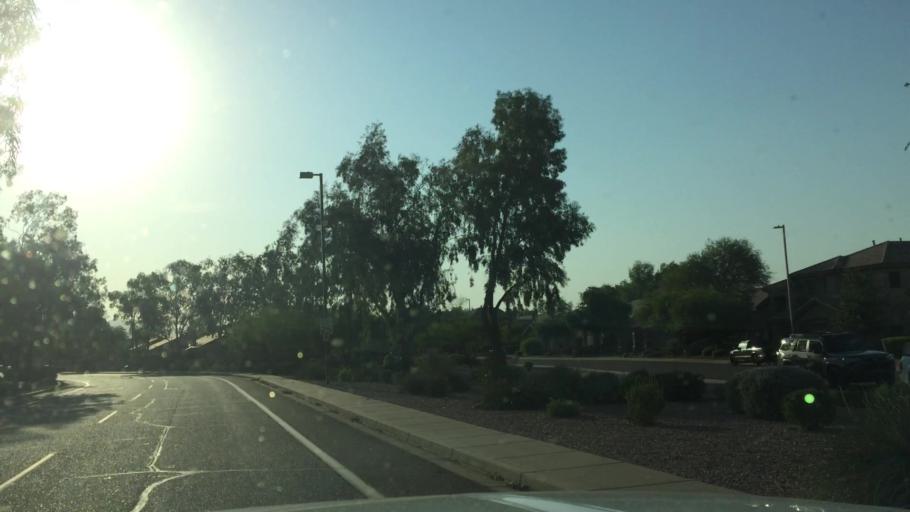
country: US
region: Arizona
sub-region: Maricopa County
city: Paradise Valley
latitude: 33.6182
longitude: -111.9369
